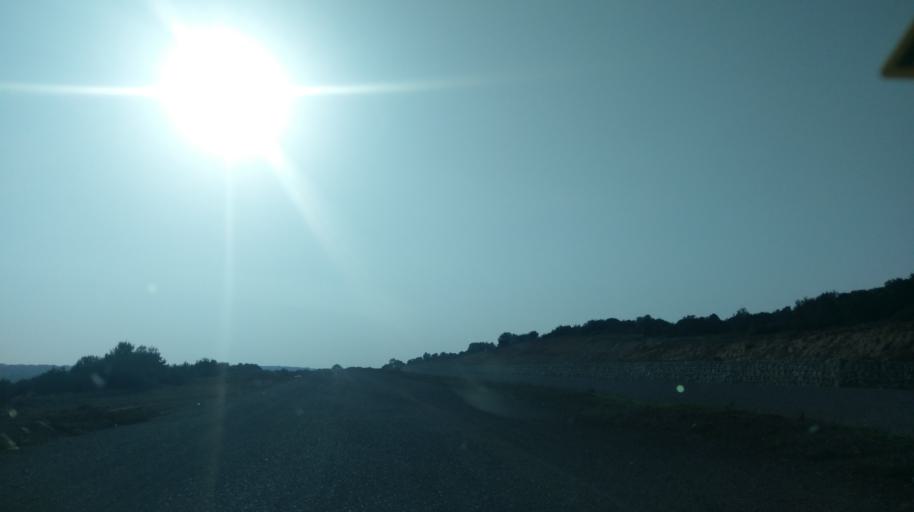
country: CY
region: Ammochostos
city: Leonarisso
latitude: 35.5153
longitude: 34.1580
